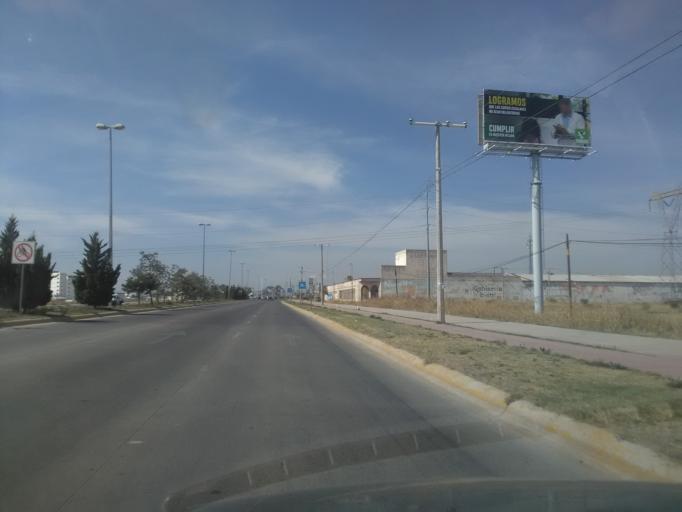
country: MX
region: Durango
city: Victoria de Durango
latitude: 24.0778
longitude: -104.5904
